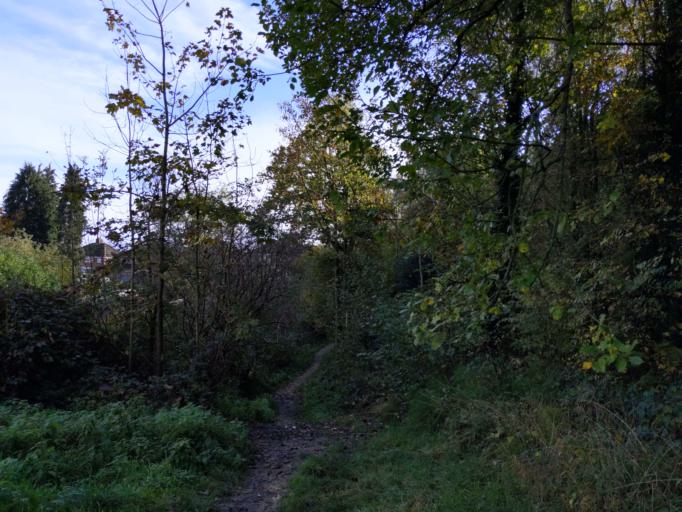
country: GB
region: England
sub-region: Oxfordshire
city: Oxford
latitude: 51.7212
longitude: -1.2528
